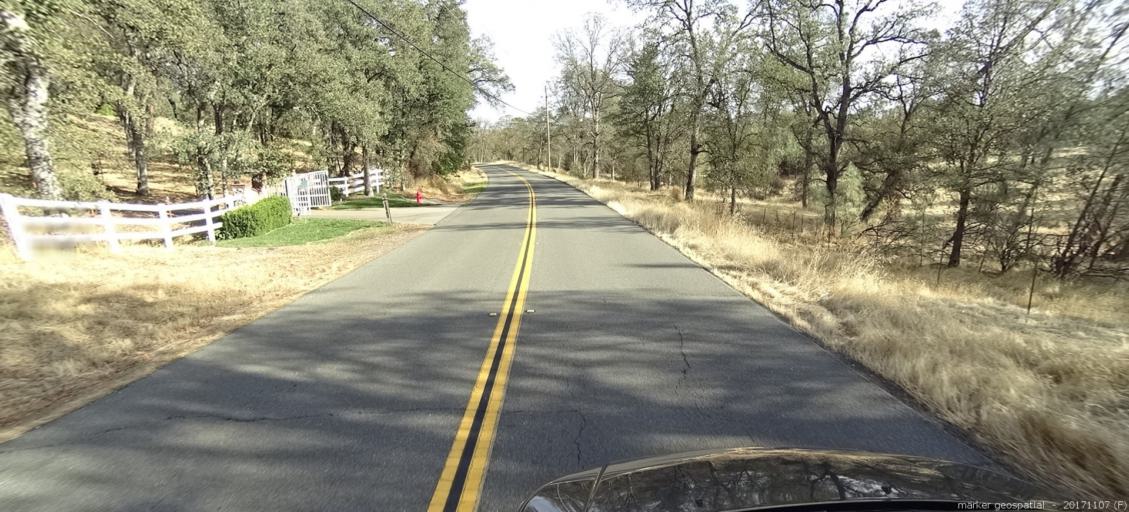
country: US
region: California
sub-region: Shasta County
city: Shasta
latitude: 40.5181
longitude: -122.4760
